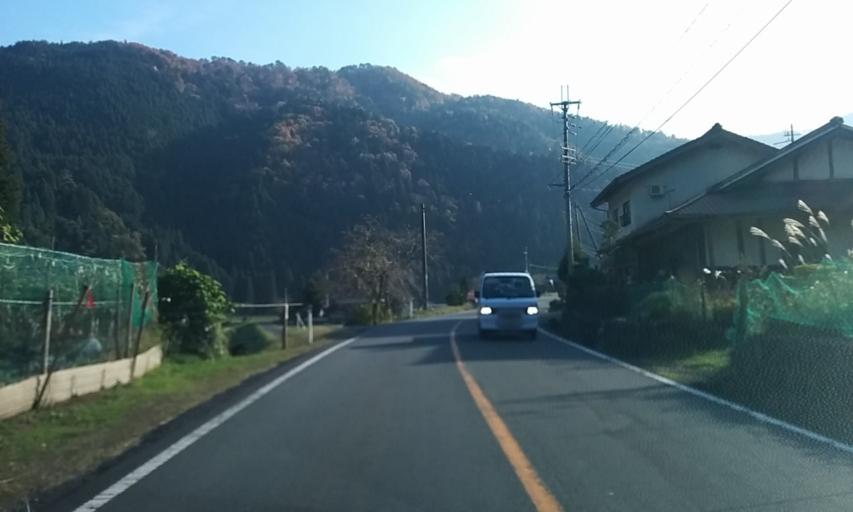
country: JP
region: Fukui
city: Obama
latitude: 35.3067
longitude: 135.6232
